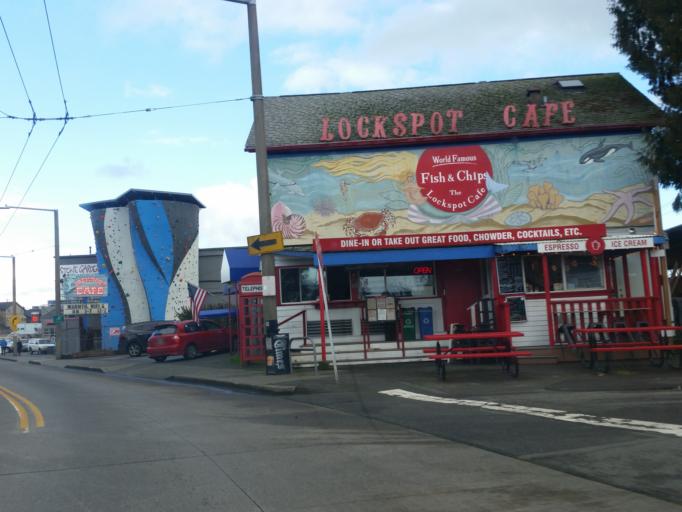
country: US
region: Washington
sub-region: King County
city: Seattle
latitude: 47.6677
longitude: -122.3963
